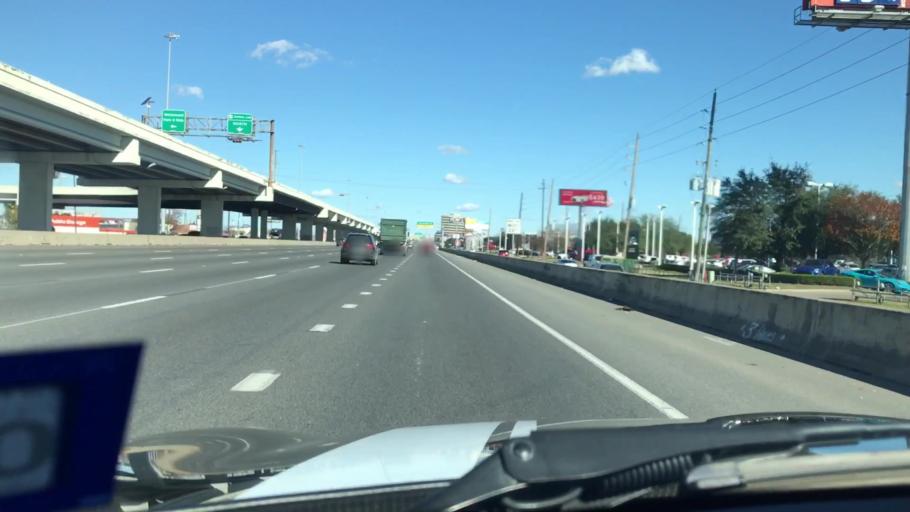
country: US
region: Texas
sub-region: Fort Bend County
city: Meadows Place
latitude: 29.6696
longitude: -95.5484
